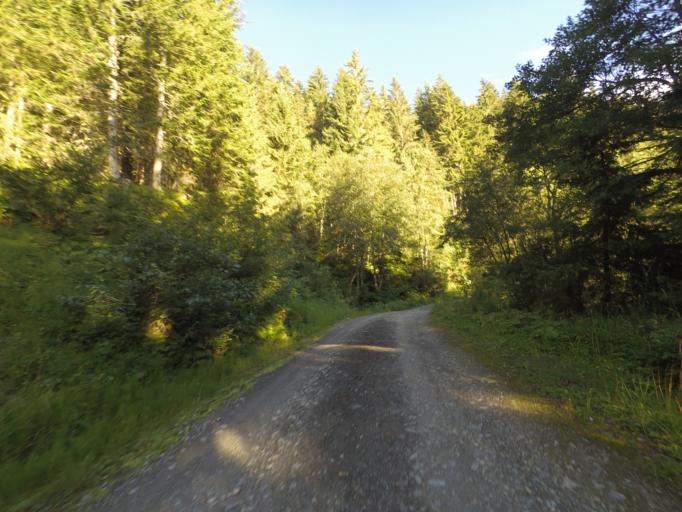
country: AT
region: Salzburg
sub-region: Politischer Bezirk Sankt Johann im Pongau
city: Goldegg
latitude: 47.3471
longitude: 13.1060
